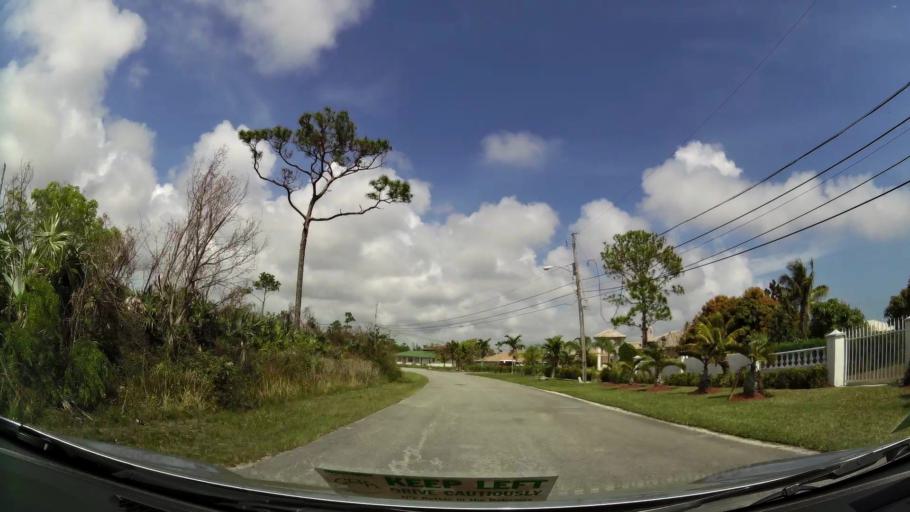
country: BS
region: Freeport
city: Freeport
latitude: 26.5041
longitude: -78.7150
